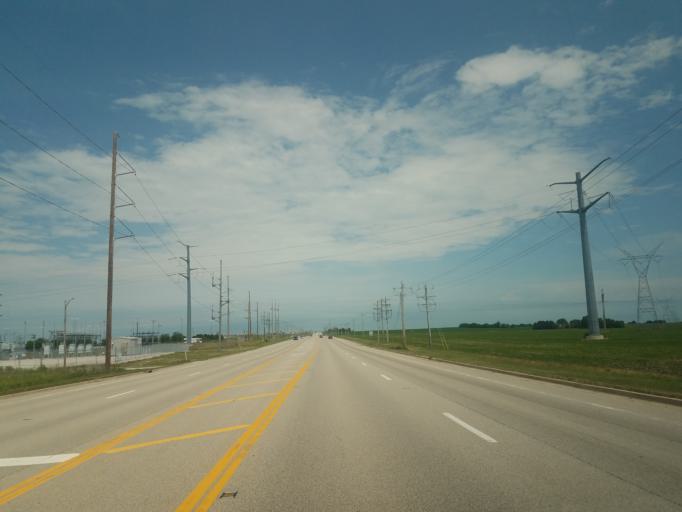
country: US
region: Illinois
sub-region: McLean County
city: Downs
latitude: 40.4521
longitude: -88.9017
